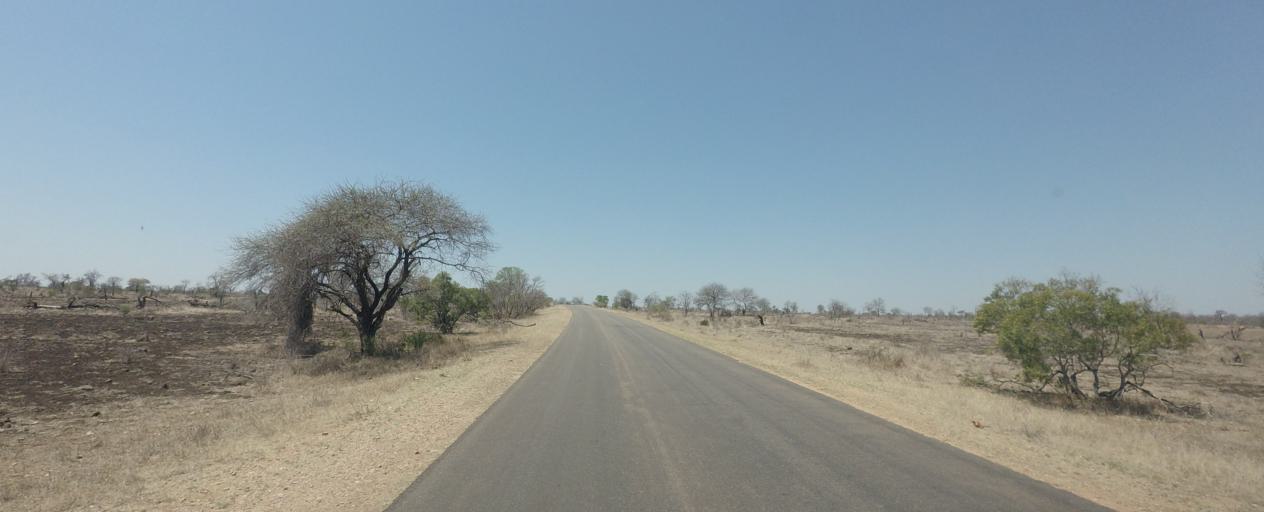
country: ZA
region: Limpopo
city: Thulamahashi
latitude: -24.4758
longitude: 31.3957
